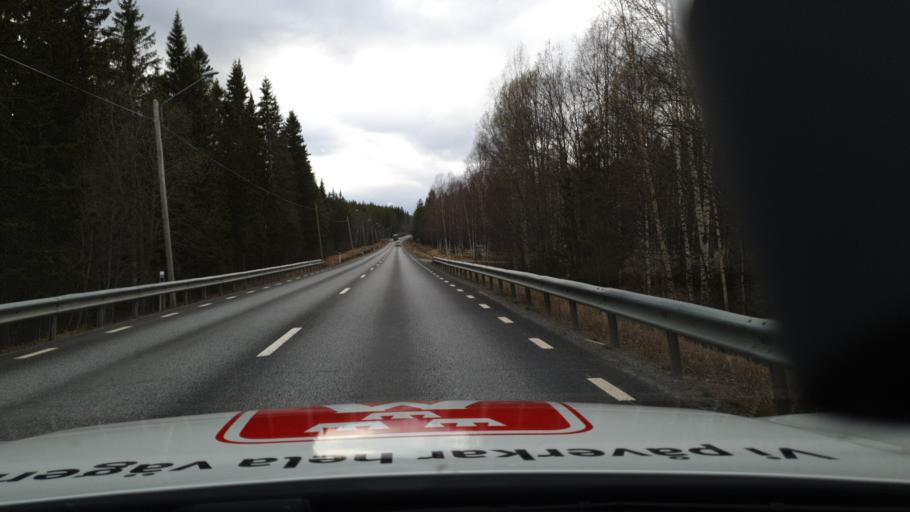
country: SE
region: Jaemtland
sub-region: OEstersunds Kommun
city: Brunflo
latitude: 63.1918
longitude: 15.1821
